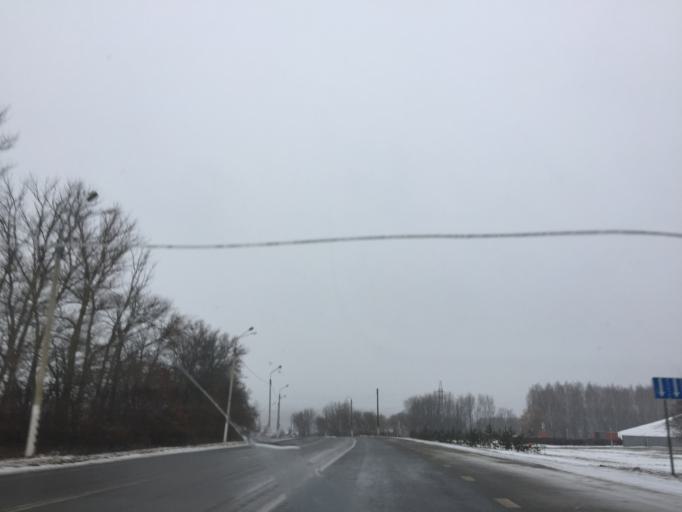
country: RU
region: Tula
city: Plavsk
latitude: 53.7248
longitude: 37.3010
